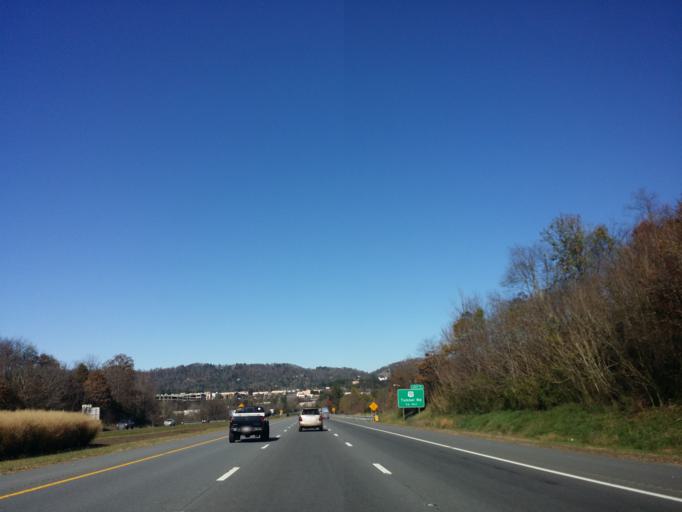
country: US
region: North Carolina
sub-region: Buncombe County
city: Biltmore Forest
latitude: 35.5726
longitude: -82.5133
